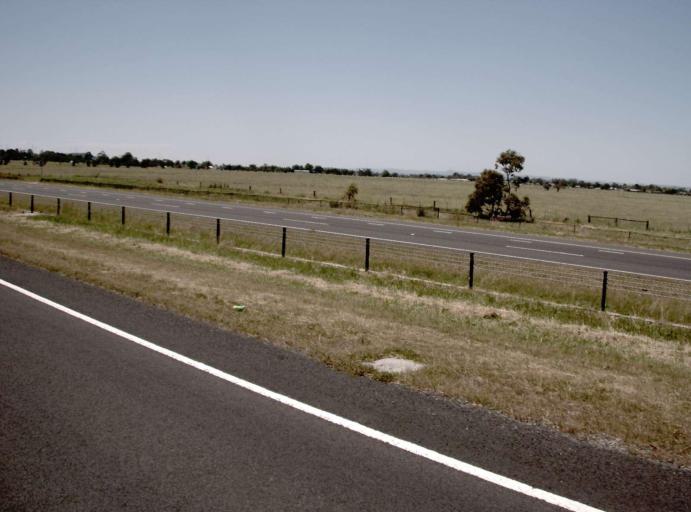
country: AU
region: Victoria
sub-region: Cardinia
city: Pakenham Upper
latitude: -38.0718
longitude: 145.5552
